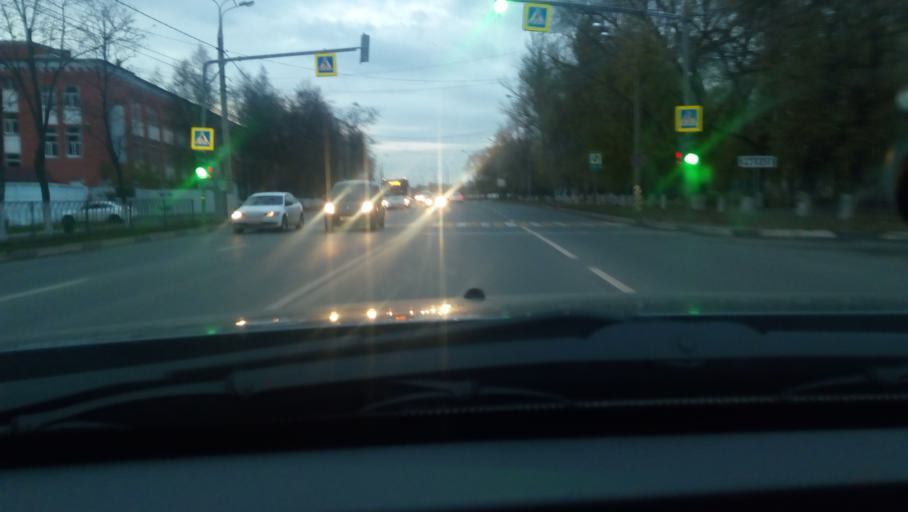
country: RU
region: Moskovskaya
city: Domodedovo
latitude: 55.4419
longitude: 37.7660
